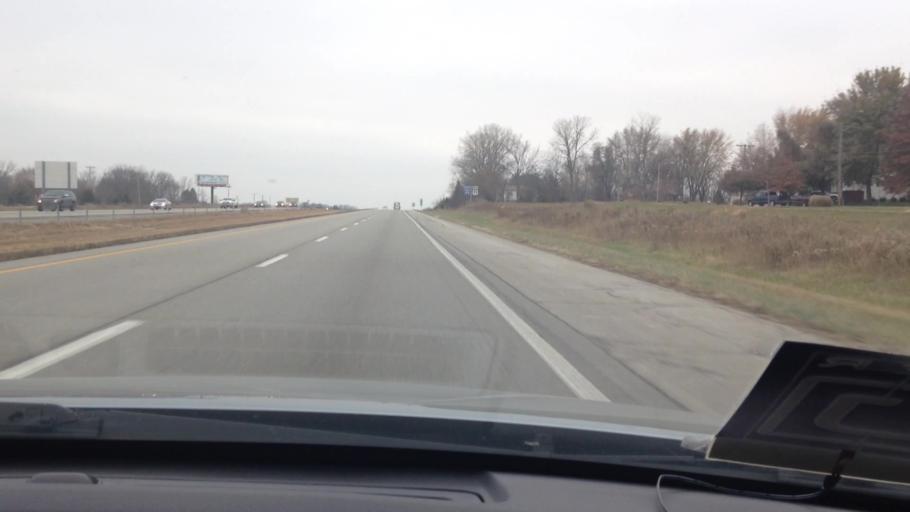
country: US
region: Missouri
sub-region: Cass County
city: Peculiar
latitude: 38.7278
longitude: -94.4592
